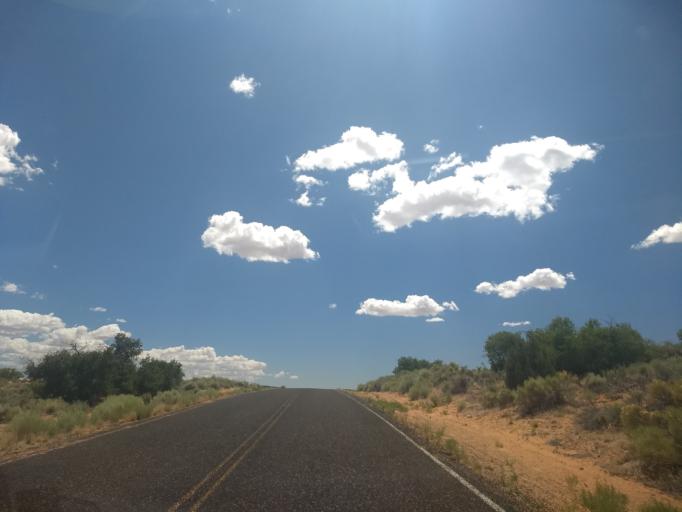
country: US
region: Utah
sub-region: Kane County
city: Kanab
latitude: 37.0420
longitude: -112.7270
